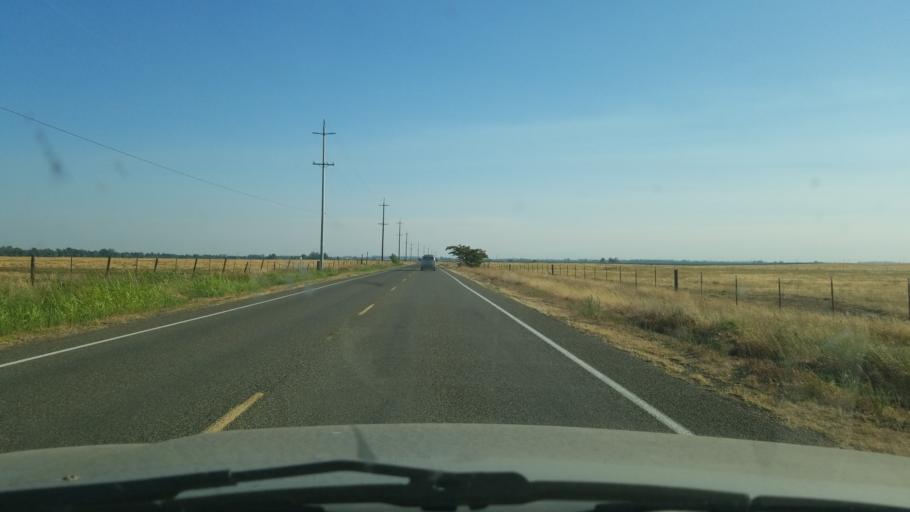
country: US
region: California
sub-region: Merced County
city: Merced
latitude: 37.4061
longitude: -120.4545
